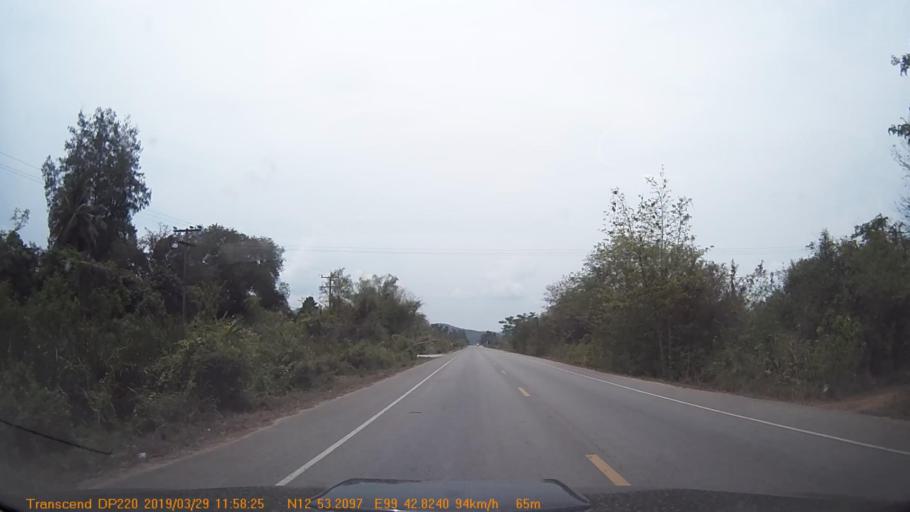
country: TH
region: Phetchaburi
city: Kaeng Krachan
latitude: 12.8864
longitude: 99.7135
